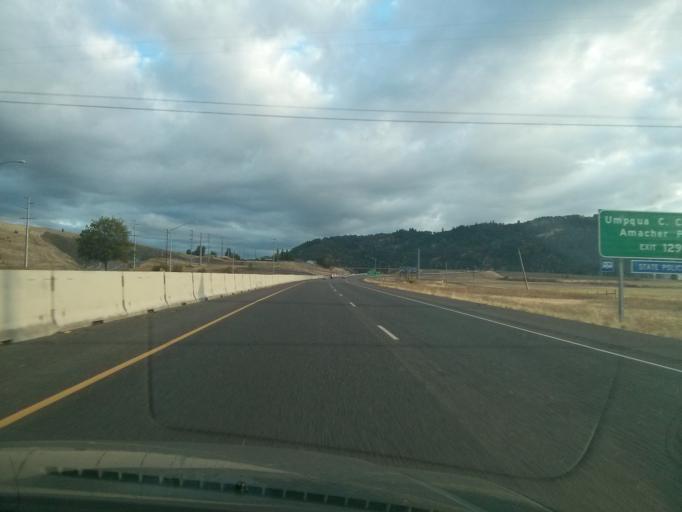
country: US
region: Oregon
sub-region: Douglas County
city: Roseburg North
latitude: 43.2977
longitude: -123.3508
